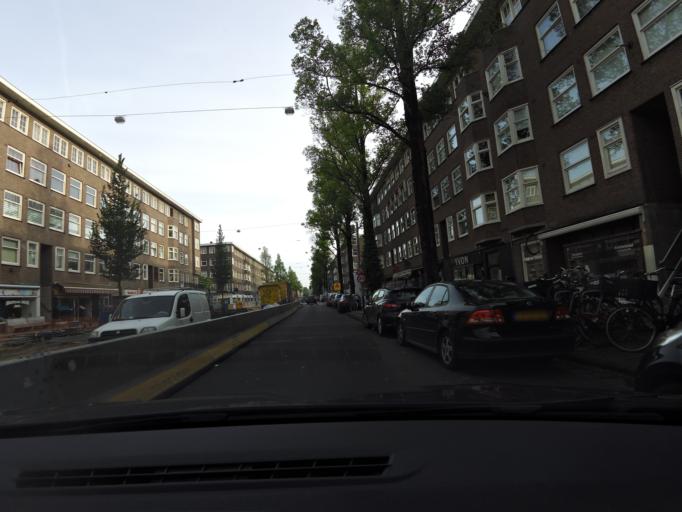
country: NL
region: North Holland
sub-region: Gemeente Ouder-Amstel
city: Duivendrecht
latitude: 52.3422
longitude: 4.9069
